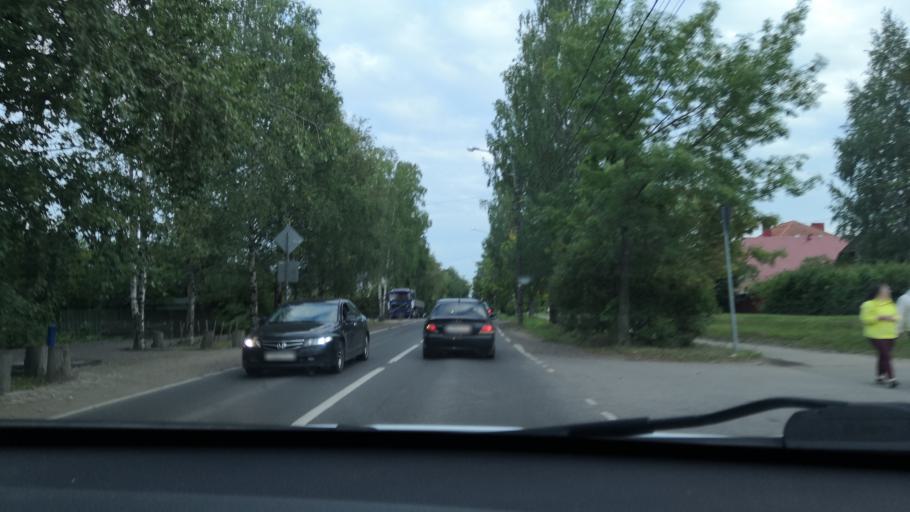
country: RU
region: St.-Petersburg
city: Pushkin
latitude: 59.7023
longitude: 30.4076
